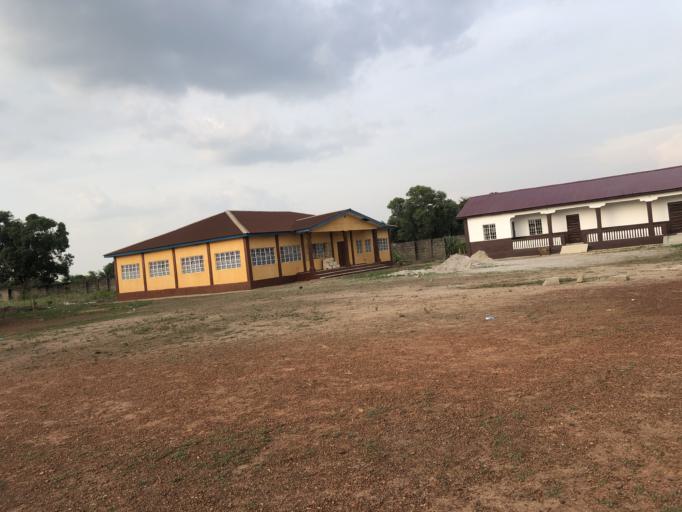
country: SL
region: Northern Province
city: Yonibana
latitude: 8.4699
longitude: -12.2039
